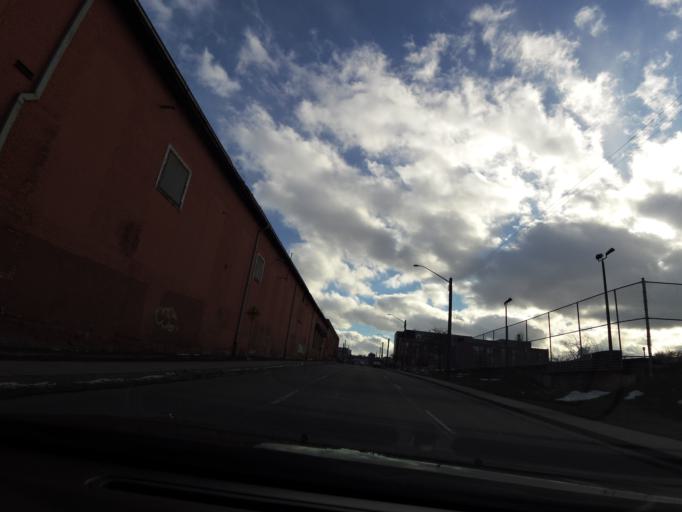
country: CA
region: Ontario
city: Hamilton
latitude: 43.2655
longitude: -79.8542
